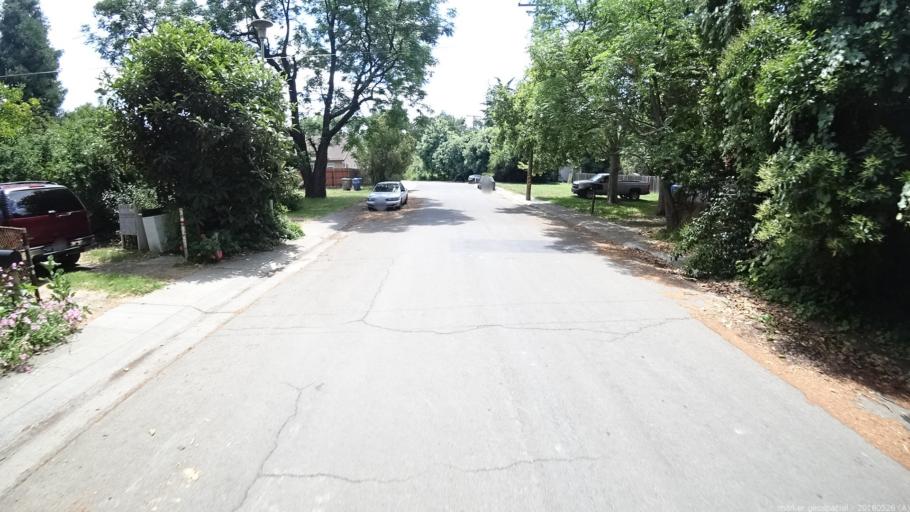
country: US
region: California
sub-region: Sacramento County
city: Sacramento
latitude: 38.6089
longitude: -121.4841
